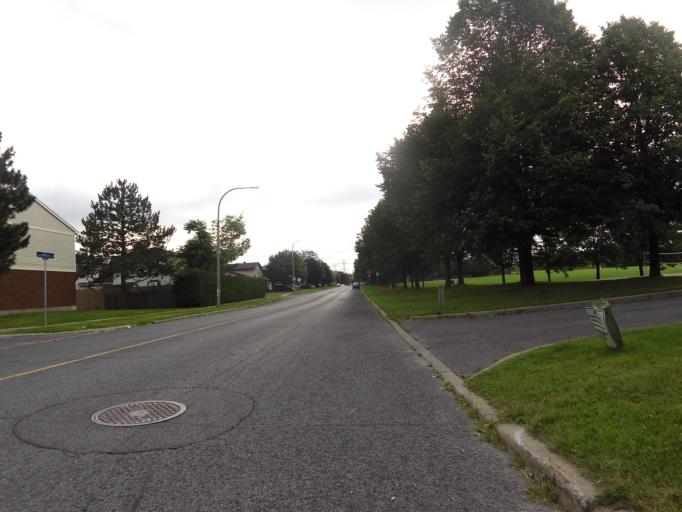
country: CA
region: Ontario
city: Bells Corners
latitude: 45.3362
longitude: -75.7462
